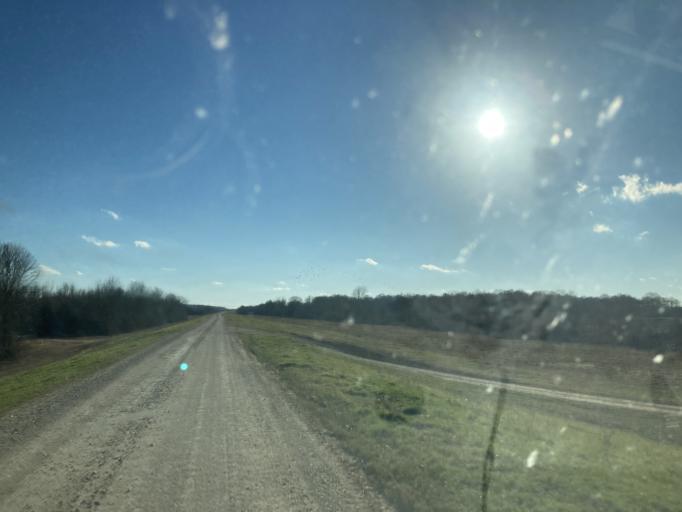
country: US
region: Mississippi
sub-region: Yazoo County
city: Yazoo City
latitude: 32.9365
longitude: -90.5465
